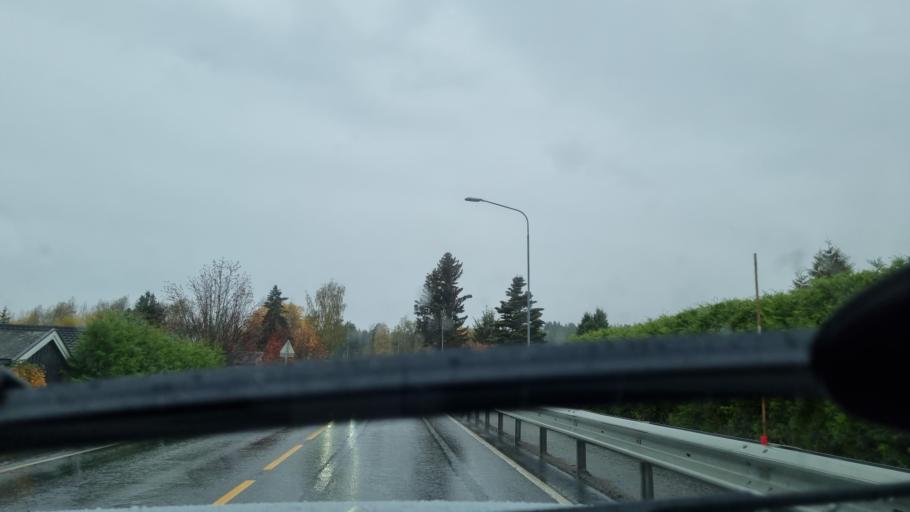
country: NO
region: Hedmark
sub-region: Hamar
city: Hamar
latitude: 60.8255
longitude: 11.0614
